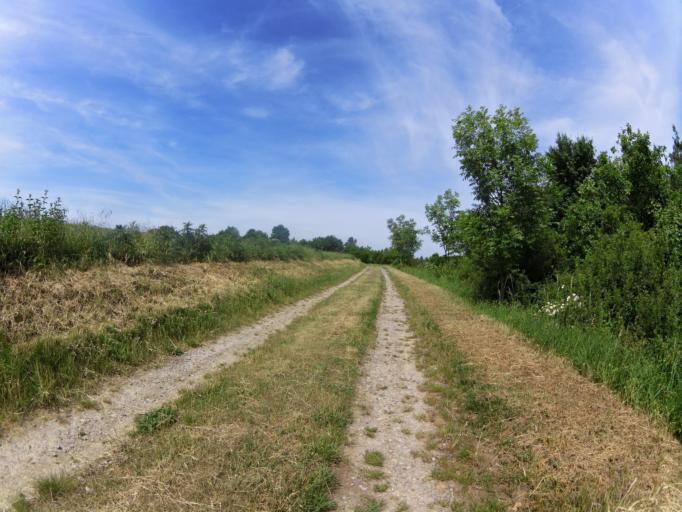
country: DE
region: Bavaria
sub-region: Regierungsbezirk Unterfranken
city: Sommerhausen
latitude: 49.6742
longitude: 10.0286
